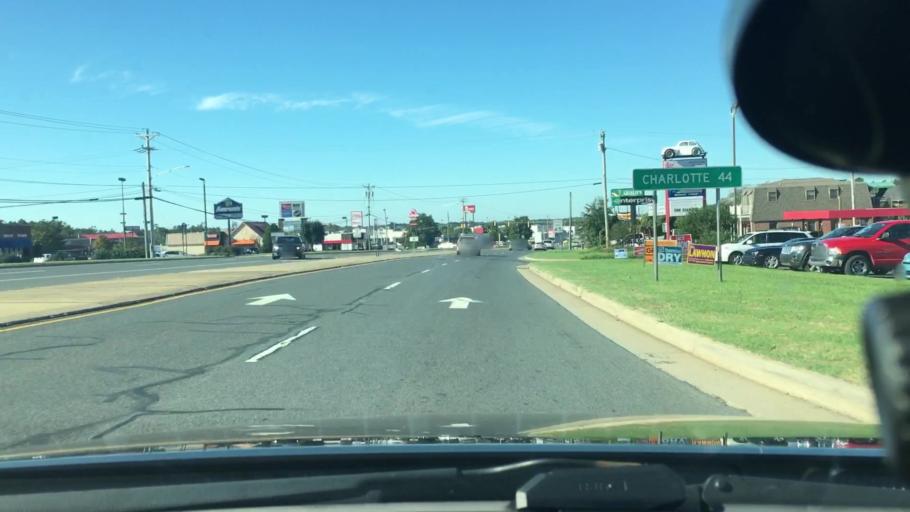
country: US
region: North Carolina
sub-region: Stanly County
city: Albemarle
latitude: 35.3456
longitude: -80.1697
